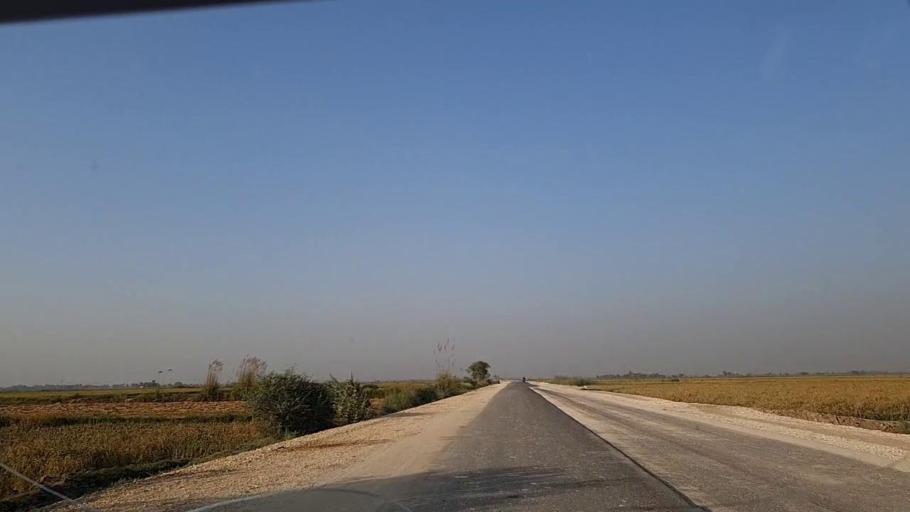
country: PK
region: Sindh
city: Rustam jo Goth
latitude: 27.9765
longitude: 68.8052
